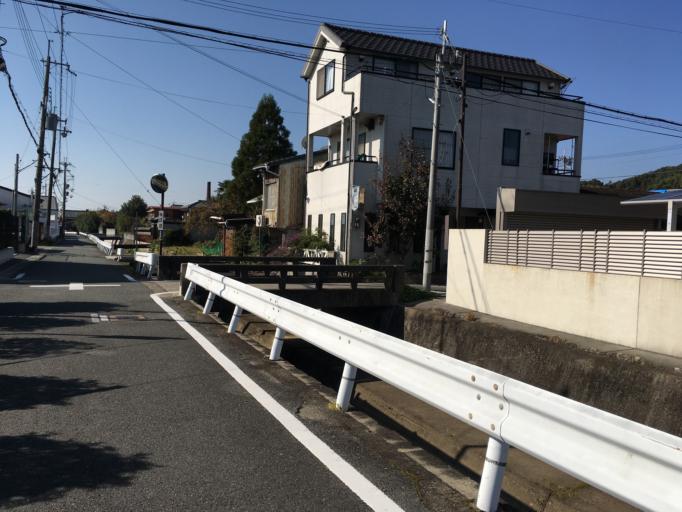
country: JP
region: Hyogo
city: Tatsunocho-tominaga
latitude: 34.8626
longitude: 134.5439
